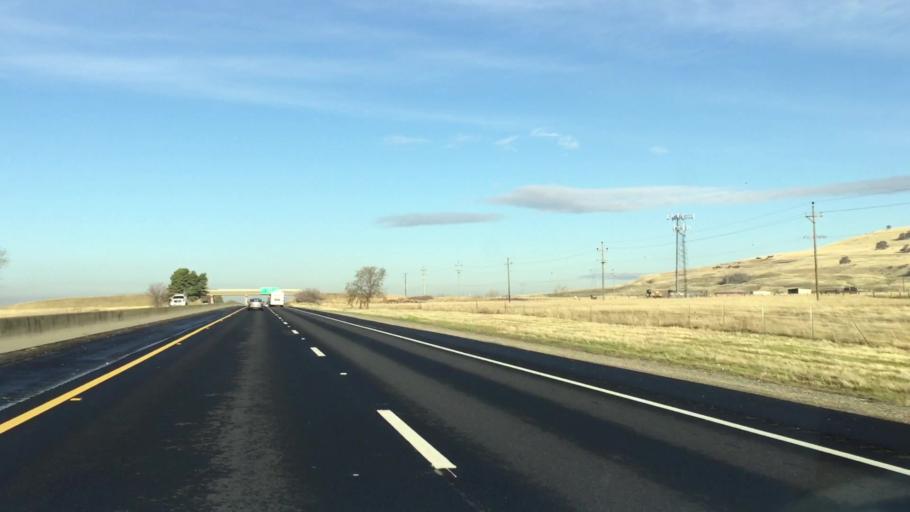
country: US
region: California
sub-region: Butte County
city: Thermalito
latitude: 39.5641
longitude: -121.6073
